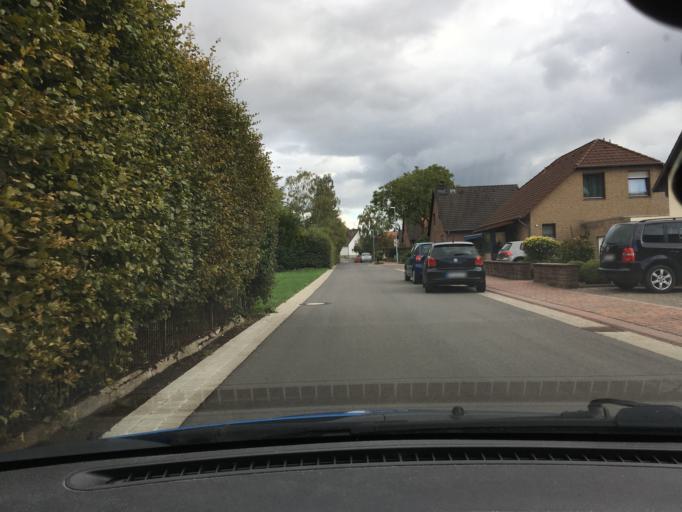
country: DE
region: Lower Saxony
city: Bad Munder am Deister
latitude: 52.2158
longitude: 9.4527
